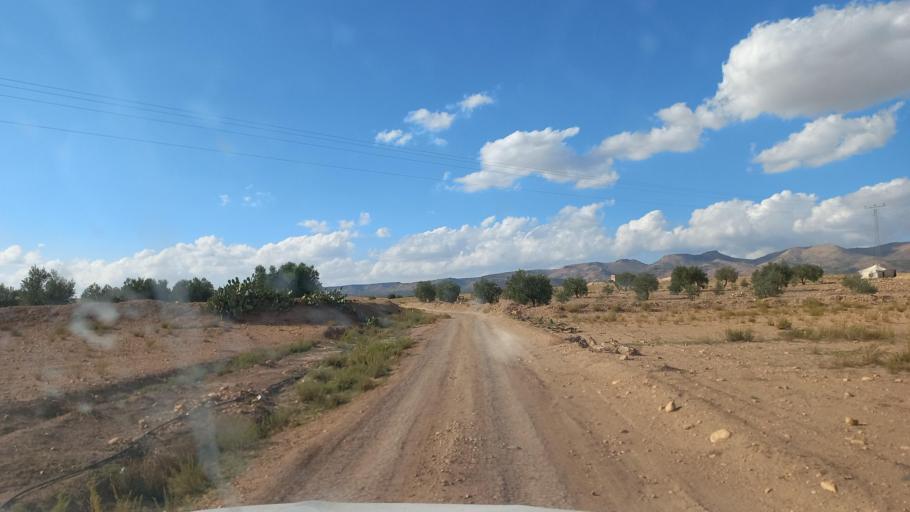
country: TN
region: Al Qasrayn
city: Sbiba
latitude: 35.3960
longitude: 9.0338
